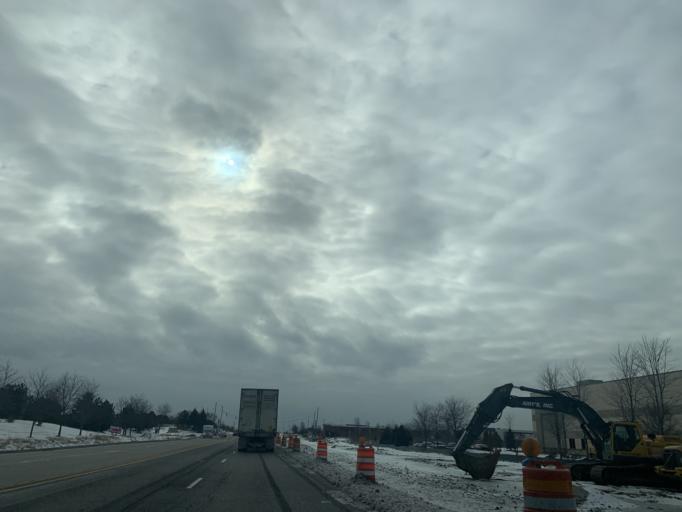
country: US
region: Illinois
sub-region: Will County
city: Romeoville
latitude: 41.6652
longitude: -88.1252
